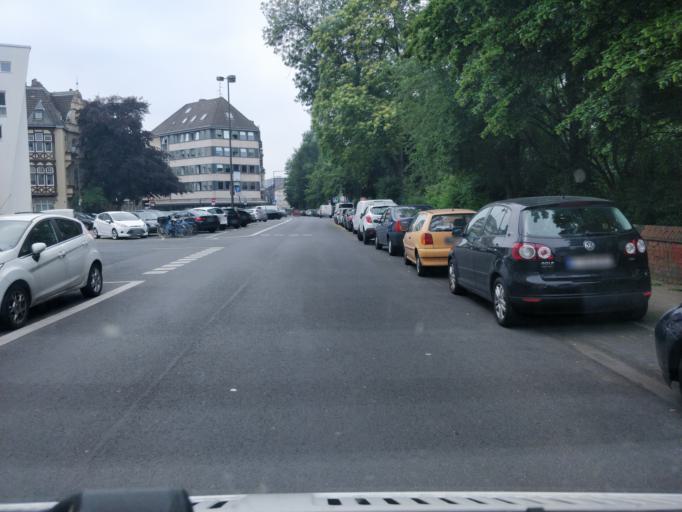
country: DE
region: North Rhine-Westphalia
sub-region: Regierungsbezirk Koln
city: Neustadt/Nord
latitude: 50.9444
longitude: 6.9384
